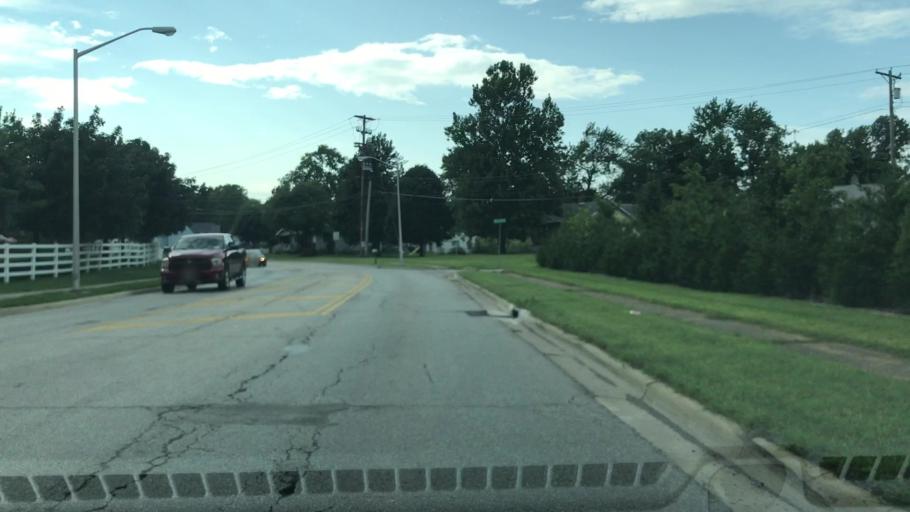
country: US
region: Ohio
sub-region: Franklin County
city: Grove City
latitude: 39.9003
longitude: -83.0696
